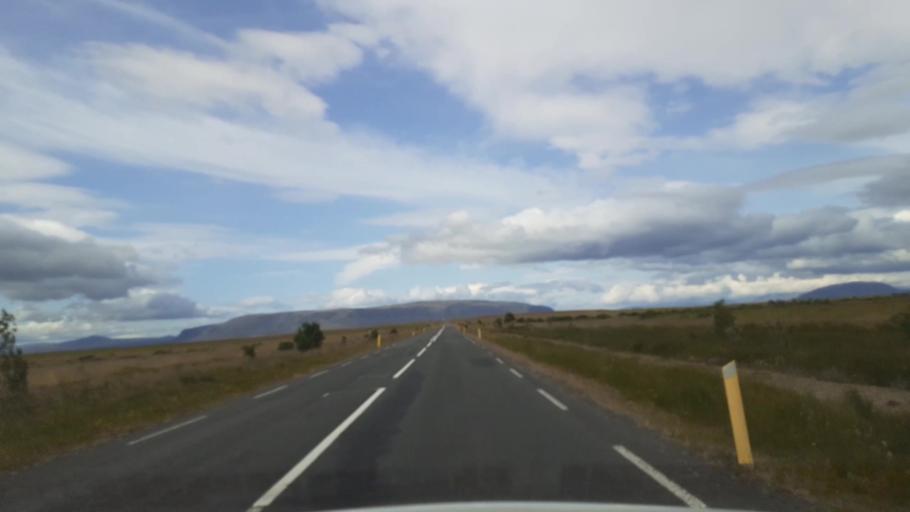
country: IS
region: South
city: Selfoss
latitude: 63.9111
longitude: -20.8301
